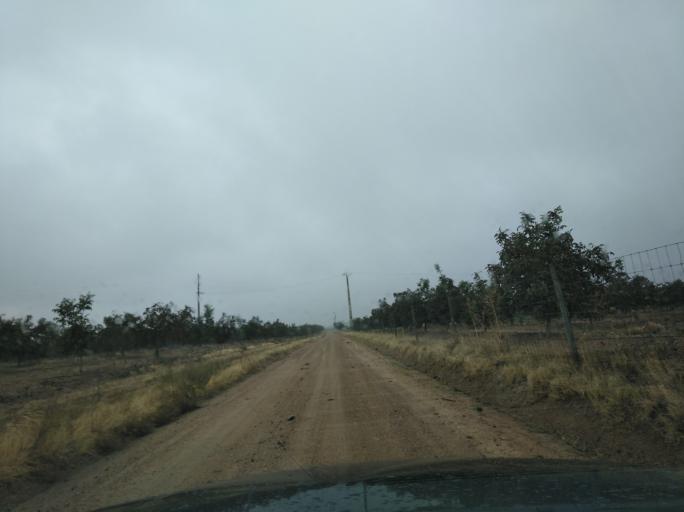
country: PT
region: Portalegre
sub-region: Campo Maior
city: Campo Maior
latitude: 38.9564
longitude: -7.0481
